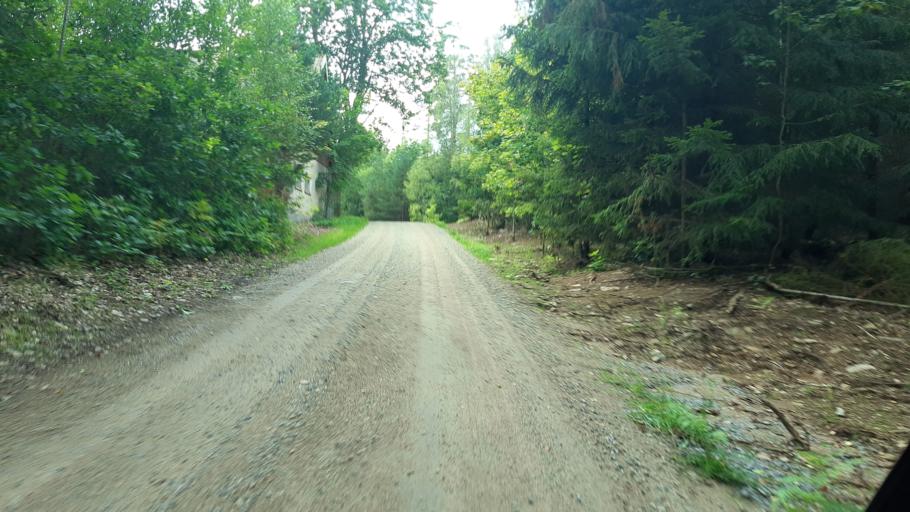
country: SE
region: Blekinge
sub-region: Ronneby Kommun
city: Brakne-Hoby
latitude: 56.4224
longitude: 15.1873
